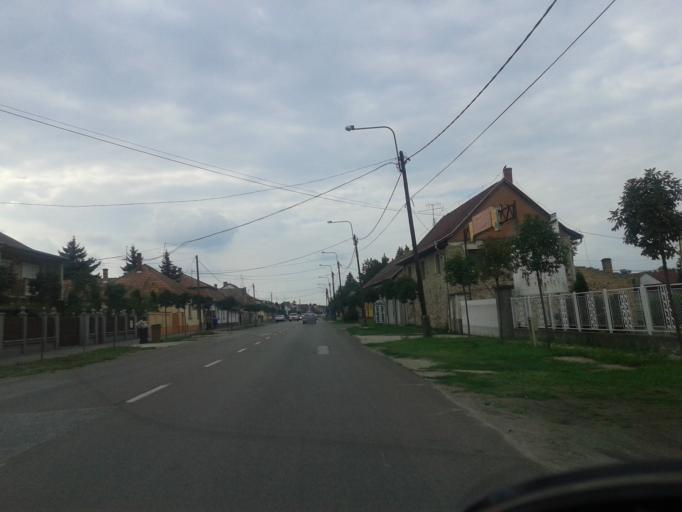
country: HU
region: Bacs-Kiskun
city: Kiskoros
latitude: 46.6134
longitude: 19.2938
